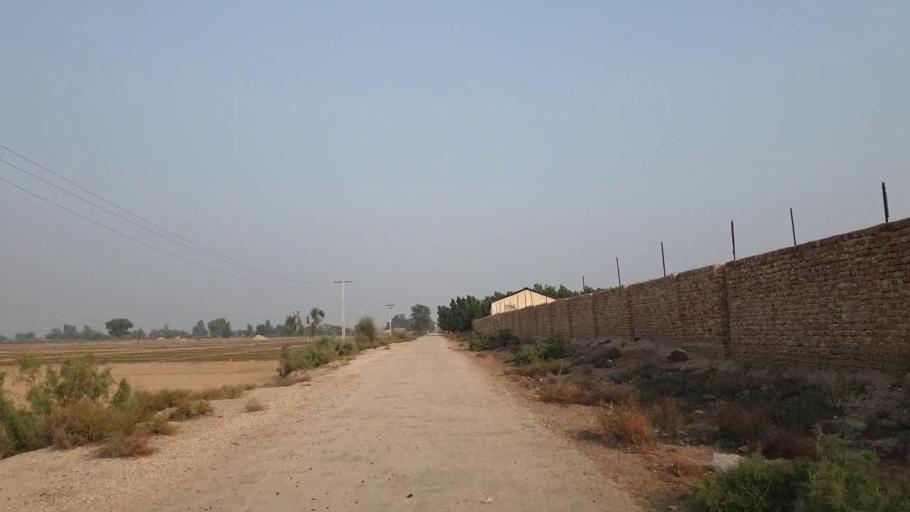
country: PK
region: Sindh
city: Bhan
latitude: 26.4888
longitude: 67.7246
